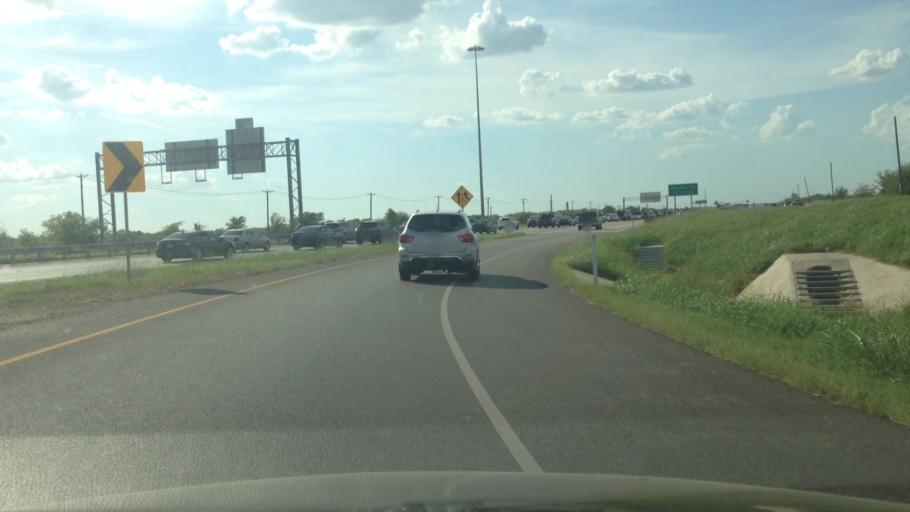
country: US
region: Texas
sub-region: Tarrant County
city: Blue Mound
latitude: 32.8896
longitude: -97.3200
